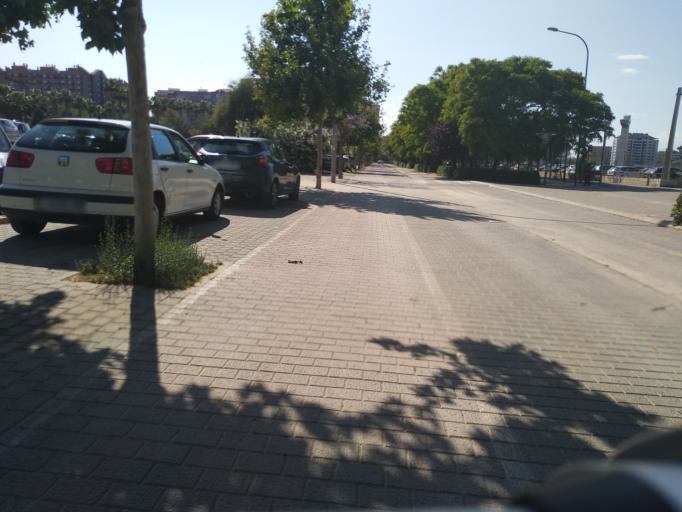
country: ES
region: Valencia
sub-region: Provincia de Valencia
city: Alboraya
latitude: 39.4786
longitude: -0.3479
